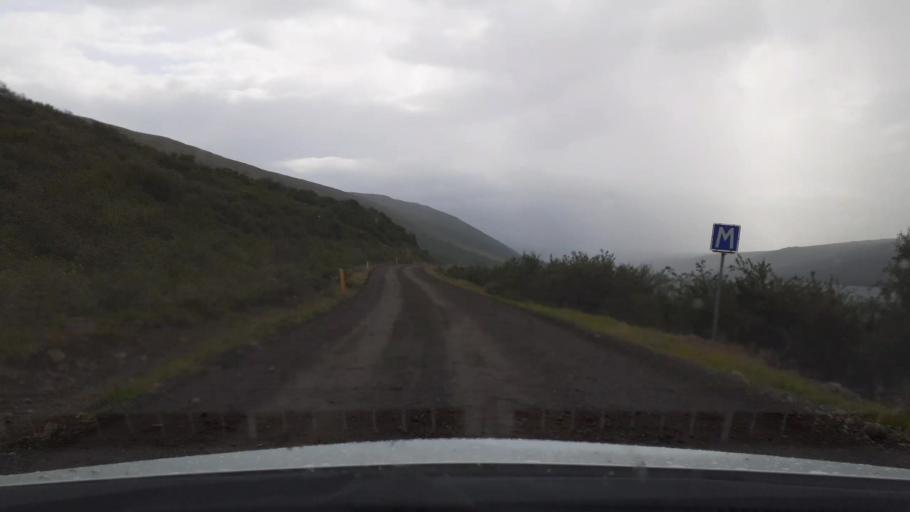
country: IS
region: Capital Region
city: Mosfellsbaer
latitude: 64.5118
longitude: -21.4012
